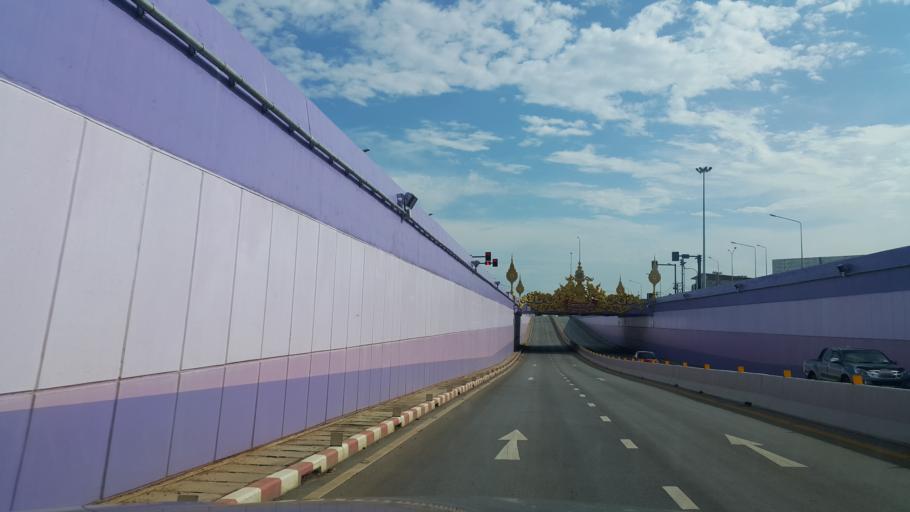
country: TH
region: Chiang Rai
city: Chiang Rai
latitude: 19.9566
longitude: 99.8780
